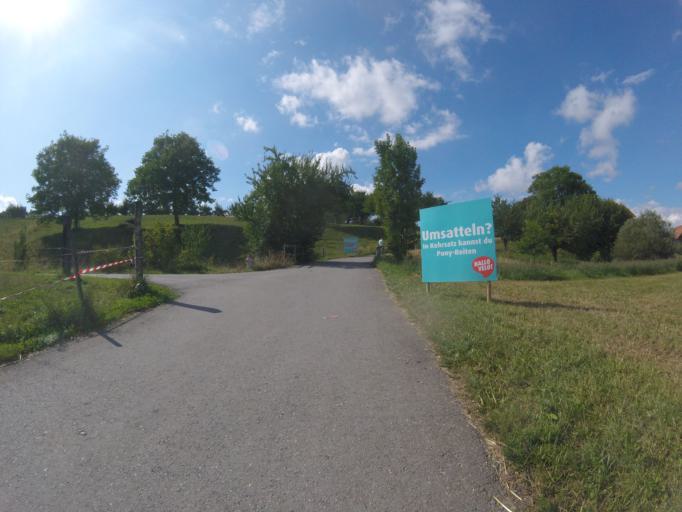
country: CH
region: Bern
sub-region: Bern-Mittelland District
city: Kehrsatz
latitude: 46.9188
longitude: 7.4798
